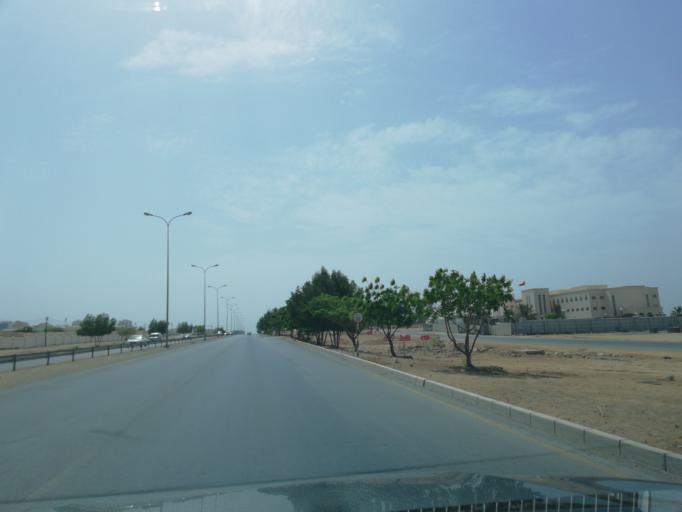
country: OM
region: Muhafazat Masqat
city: Bawshar
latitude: 23.5830
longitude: 58.3559
